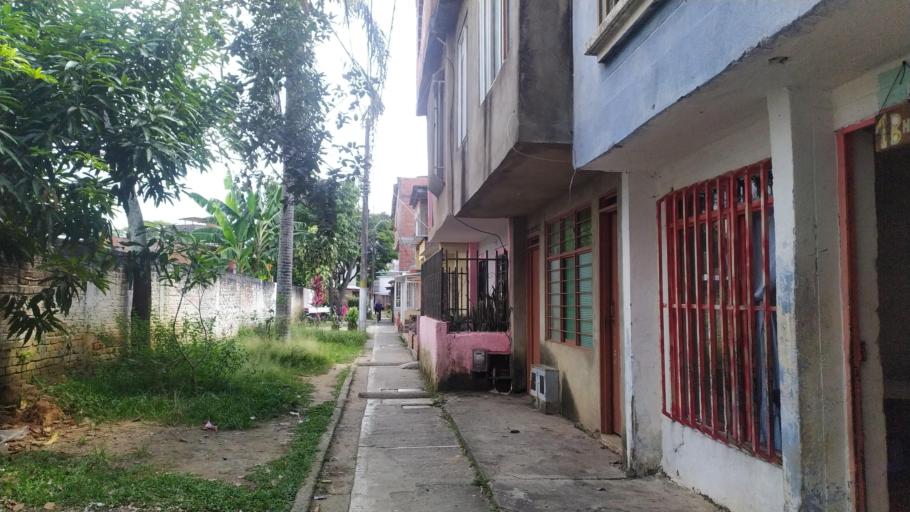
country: CO
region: Valle del Cauca
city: Jamundi
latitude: 3.2533
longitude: -76.5435
